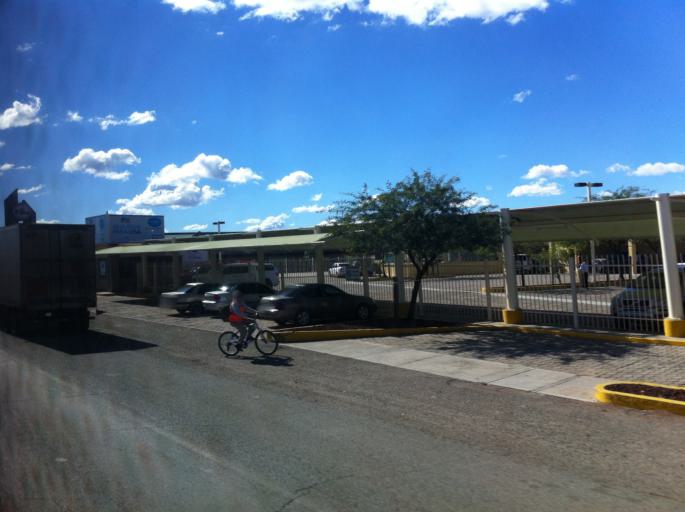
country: MX
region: Sonora
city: Santa Ana
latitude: 30.5404
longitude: -111.1133
